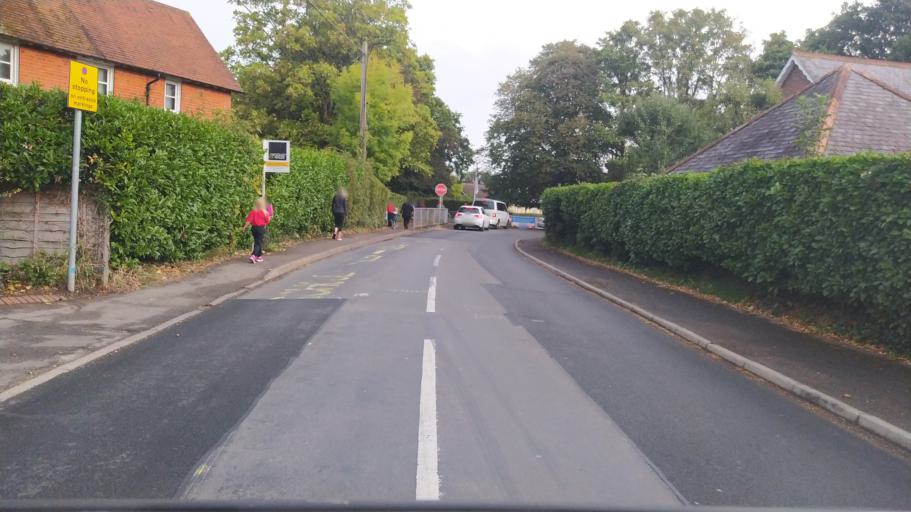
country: GB
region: England
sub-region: Hampshire
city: Romsey
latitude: 51.0154
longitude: -1.5449
